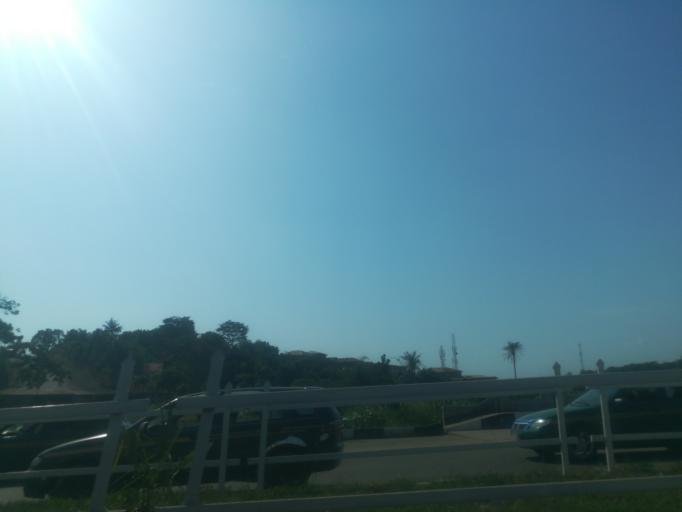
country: NG
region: Ogun
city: Abeokuta
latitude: 7.1452
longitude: 3.3420
